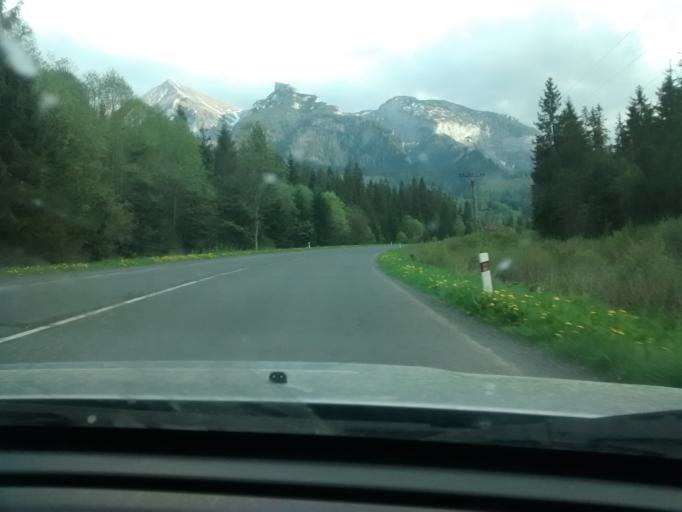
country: PL
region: Lesser Poland Voivodeship
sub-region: Powiat tatrzanski
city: Bukowina Tatrzanska
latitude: 49.2872
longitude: 20.1750
